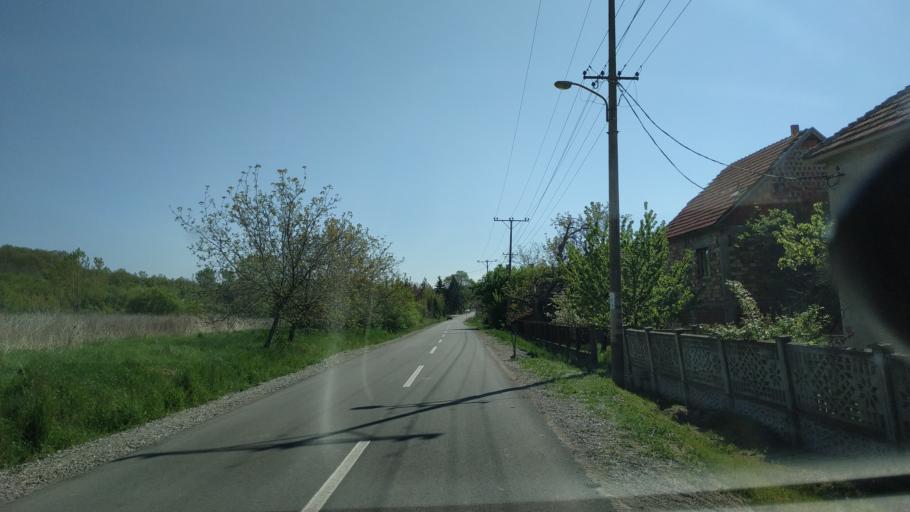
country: RS
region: Central Serbia
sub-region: Nisavski Okrug
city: Nis
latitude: 43.4556
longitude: 21.8523
